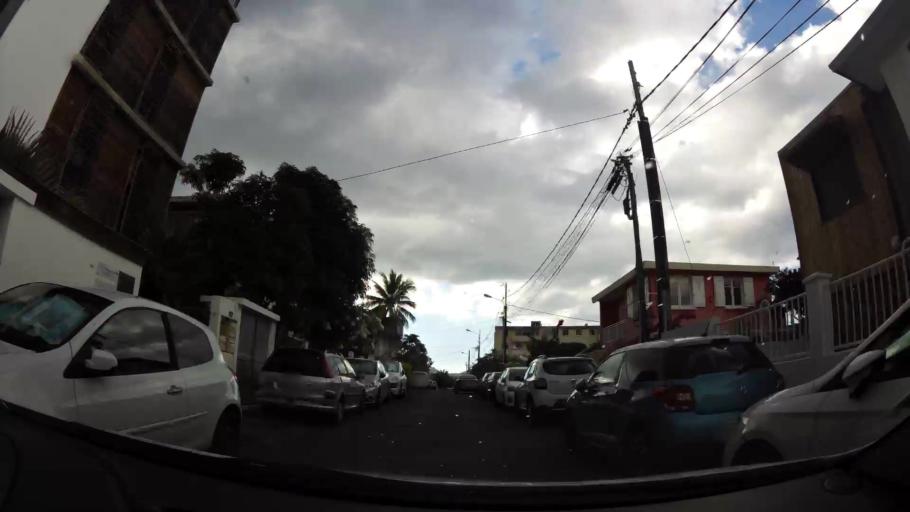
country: RE
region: Reunion
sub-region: Reunion
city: Saint-Denis
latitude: -20.8893
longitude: 55.4591
